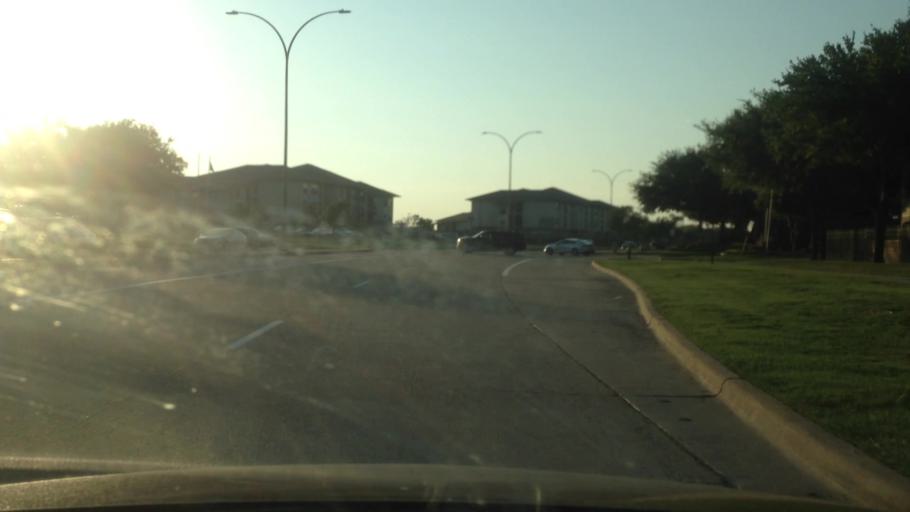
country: US
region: Texas
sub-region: Tarrant County
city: Dalworthington Gardens
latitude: 32.6453
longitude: -97.1237
